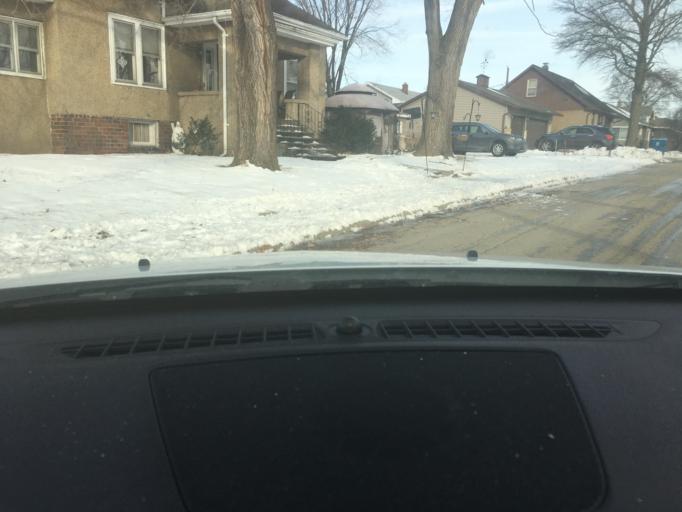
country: US
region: Illinois
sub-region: LaSalle County
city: Peru
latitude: 41.3337
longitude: -89.1144
